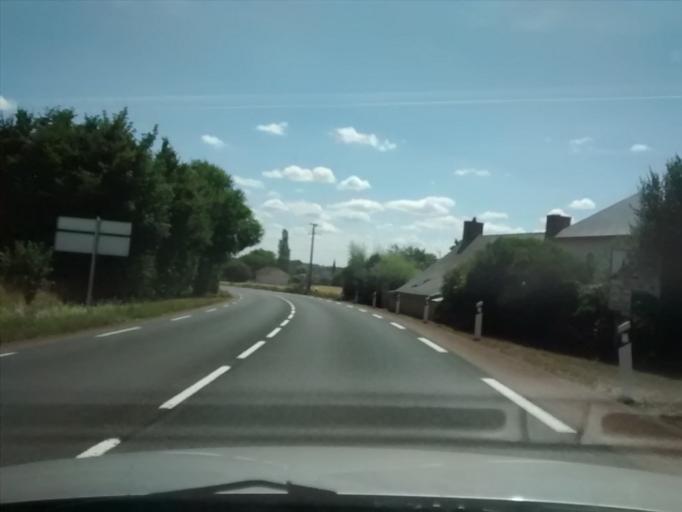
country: FR
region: Pays de la Loire
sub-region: Departement de la Sarthe
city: Loue
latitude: 48.0214
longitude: -0.0846
